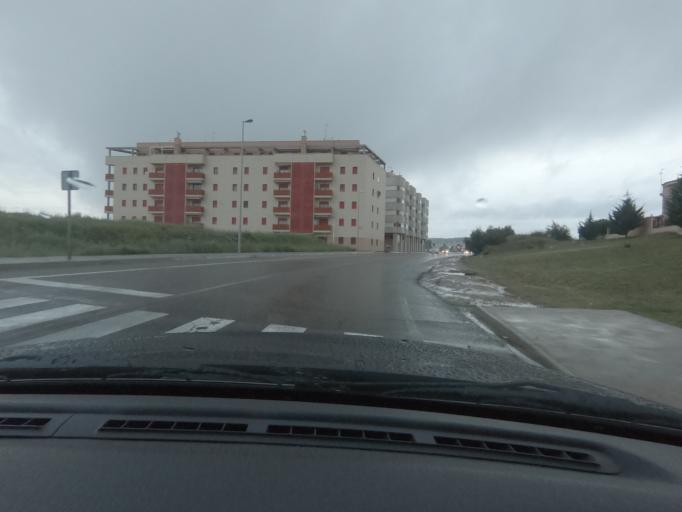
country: ES
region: Extremadura
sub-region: Provincia de Badajoz
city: Merida
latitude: 38.9327
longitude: -6.3412
